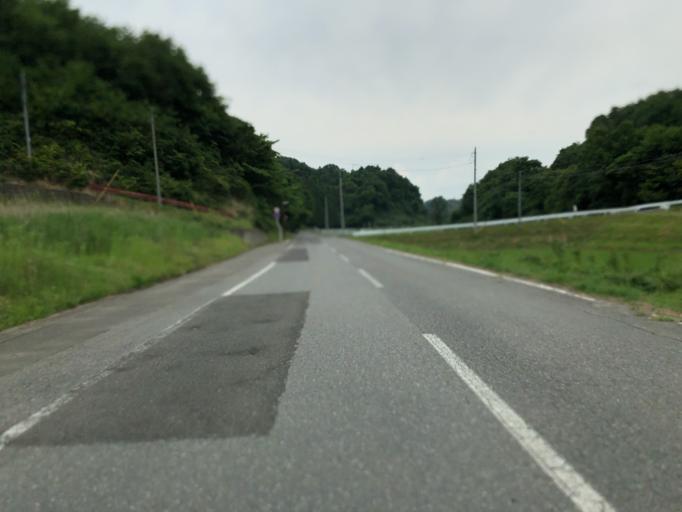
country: JP
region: Fukushima
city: Miharu
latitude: 37.4614
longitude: 140.5232
